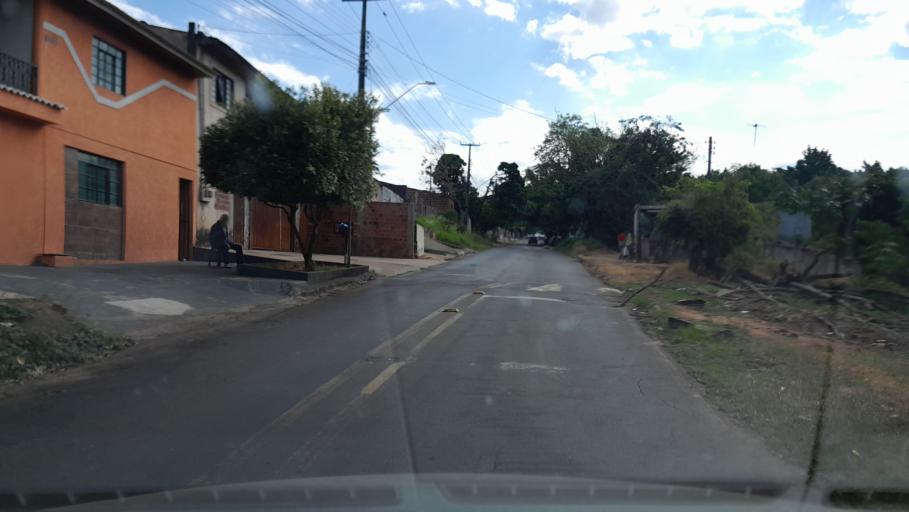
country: BR
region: Parana
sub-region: Umuarama
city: Umuarama
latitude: -23.7727
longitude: -53.3046
